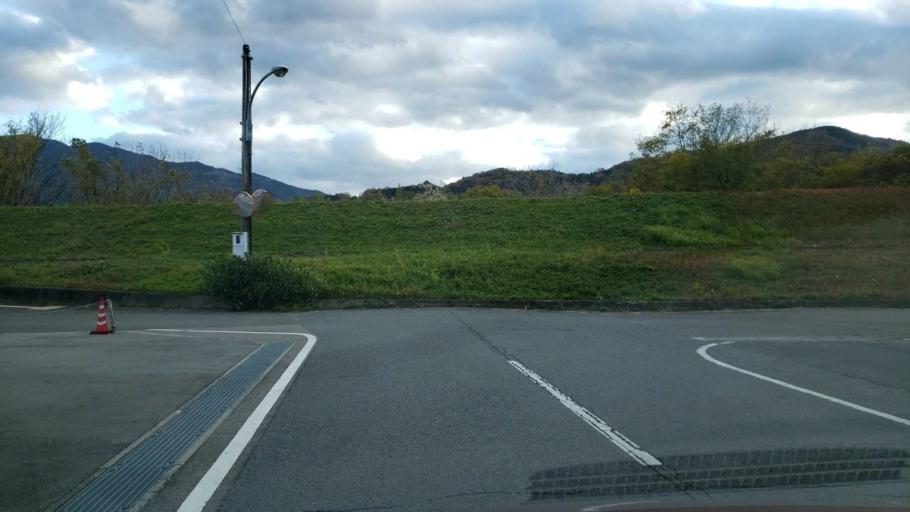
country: JP
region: Tokushima
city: Wakimachi
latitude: 34.0616
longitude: 134.1635
